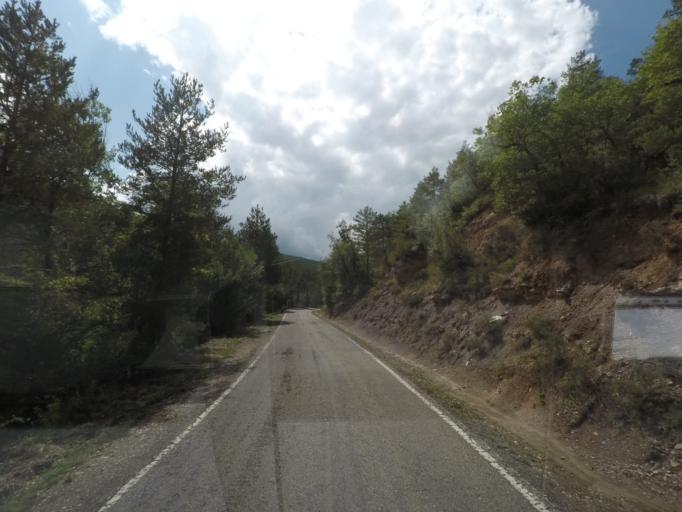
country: ES
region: Aragon
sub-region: Provincia de Huesca
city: Yebra de Basa
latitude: 42.4066
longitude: -0.2324
